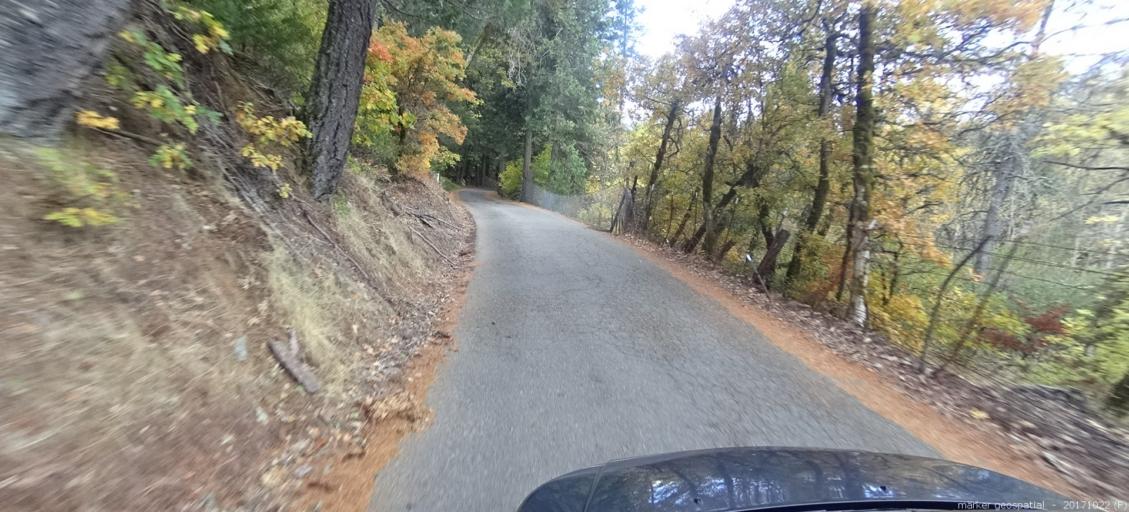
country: US
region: California
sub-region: Siskiyou County
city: Dunsmuir
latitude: 41.1689
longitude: -122.2838
